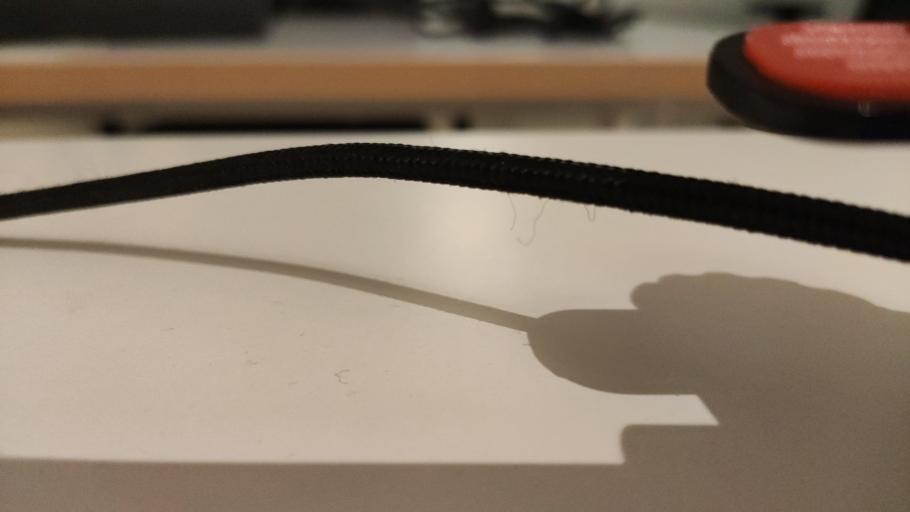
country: RU
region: Moskovskaya
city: Mikhnevo
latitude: 55.0885
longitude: 37.9874
